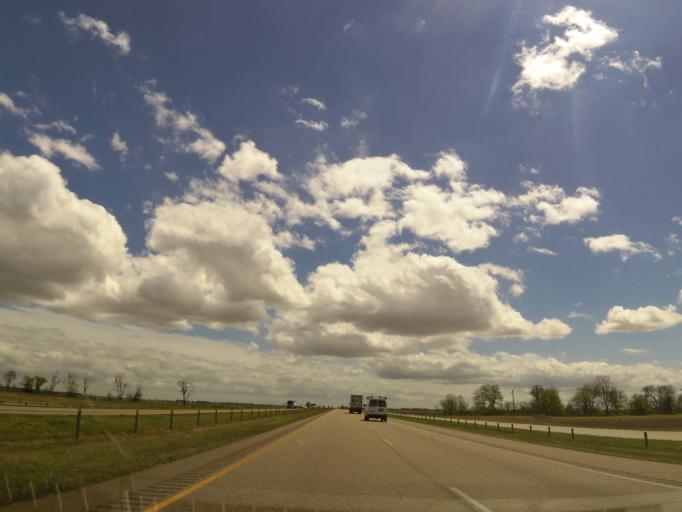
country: US
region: Arkansas
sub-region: Crittenden County
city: Marion
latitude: 35.3452
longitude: -90.2719
